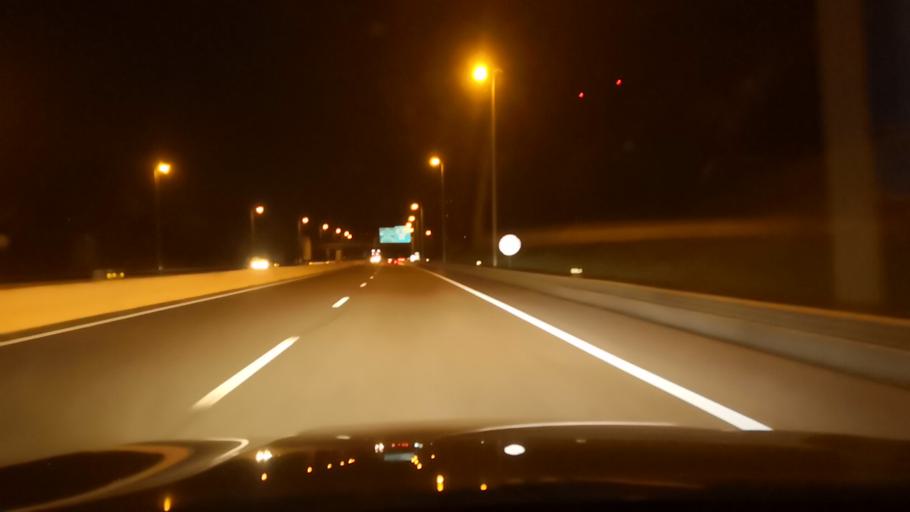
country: PT
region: Setubal
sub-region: Palmela
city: Palmela
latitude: 38.5714
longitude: -8.8663
